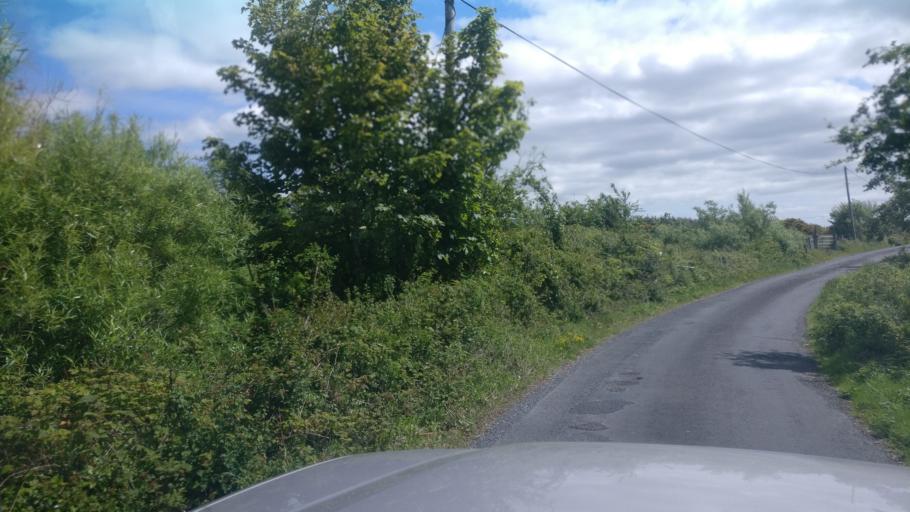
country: IE
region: Connaught
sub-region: County Galway
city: Gort
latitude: 53.1246
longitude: -8.7035
